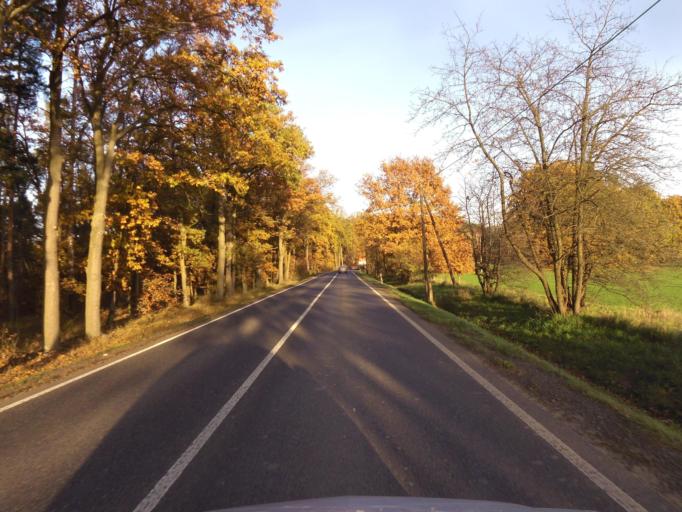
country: CZ
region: Liberecky
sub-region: Okres Ceska Lipa
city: Ceska Lipa
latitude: 50.6372
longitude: 14.4981
